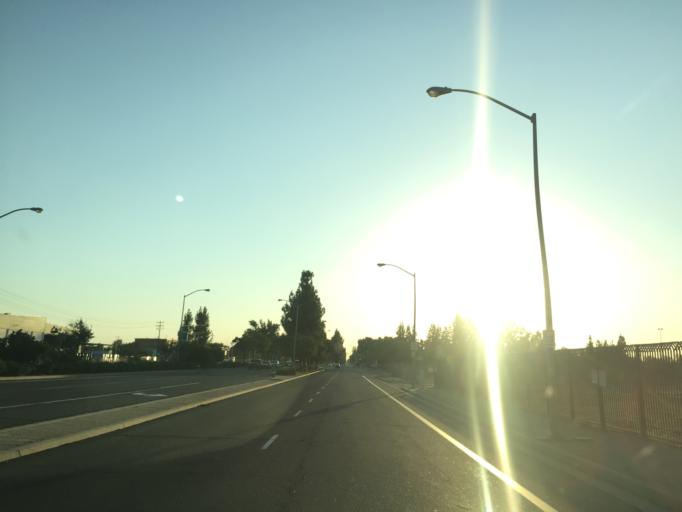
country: US
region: California
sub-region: Fresno County
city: Sunnyside
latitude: 36.7653
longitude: -119.7150
